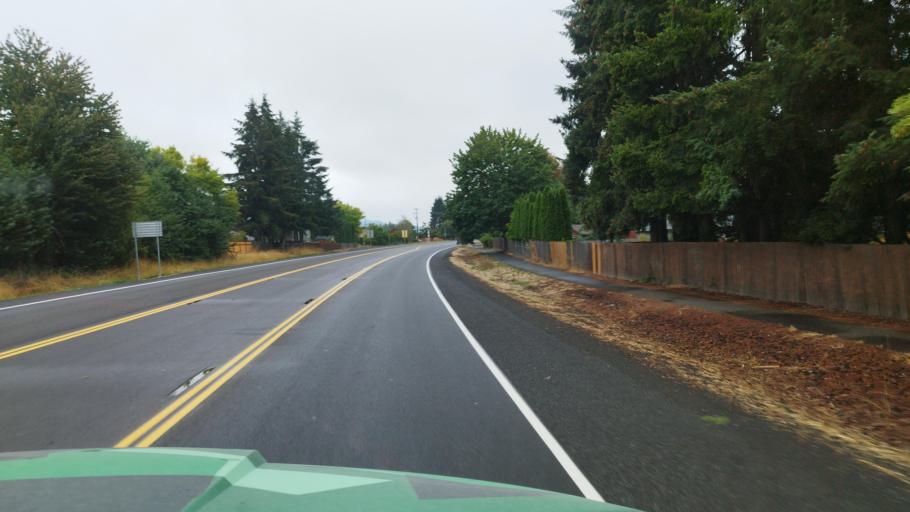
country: US
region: Oregon
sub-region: Washington County
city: Cornelius
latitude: 45.5174
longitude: -123.0851
